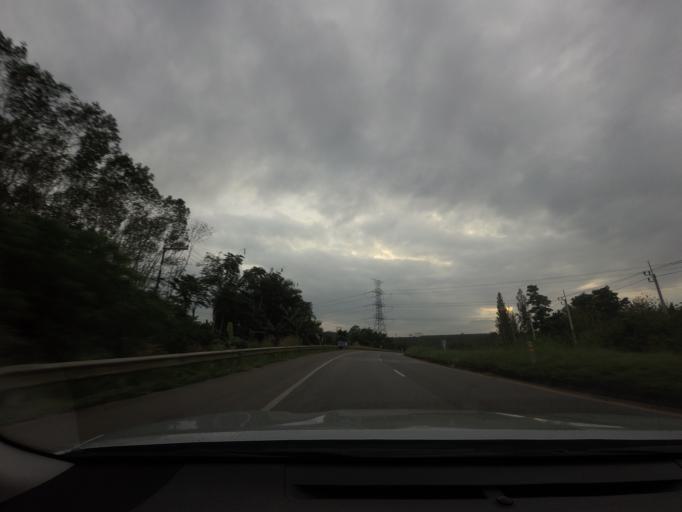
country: TH
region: Surat Thani
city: Phunphin
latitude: 9.0370
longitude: 99.1047
